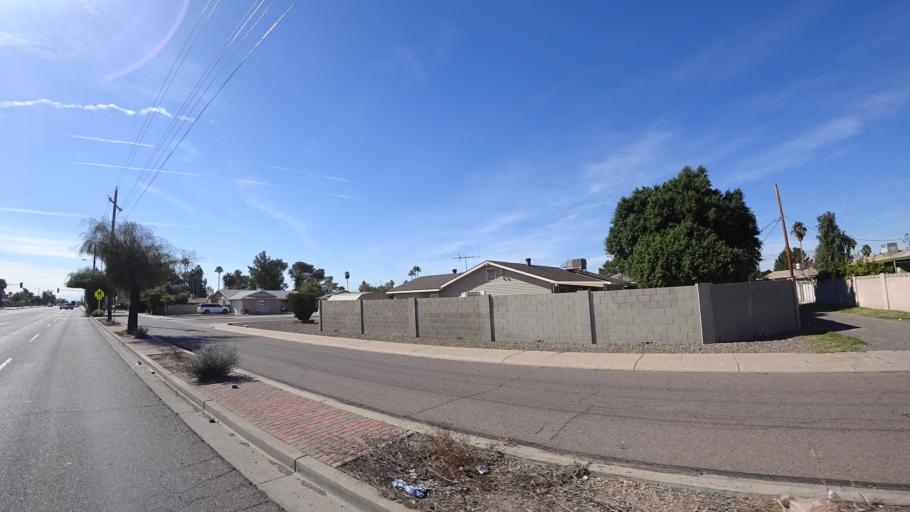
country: US
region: Arizona
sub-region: Maricopa County
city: Glendale
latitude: 33.5035
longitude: -112.1865
